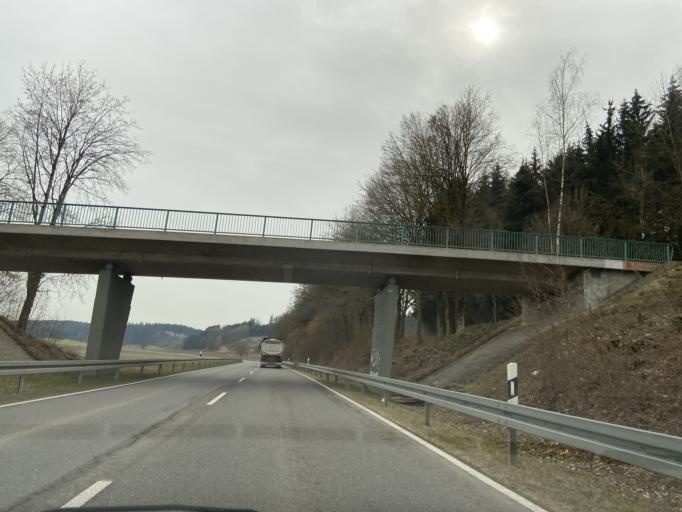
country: DE
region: Baden-Wuerttemberg
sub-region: Tuebingen Region
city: Ostrach
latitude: 47.9724
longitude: 9.3472
